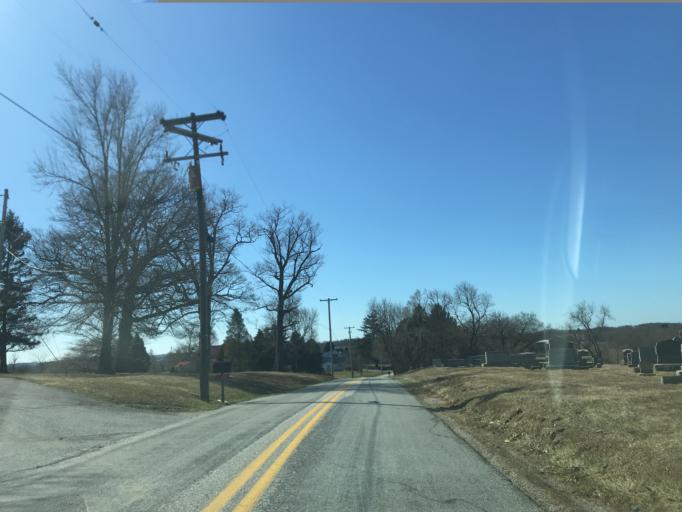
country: US
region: Pennsylvania
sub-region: York County
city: Stewartstown
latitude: 39.7237
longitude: -76.5226
